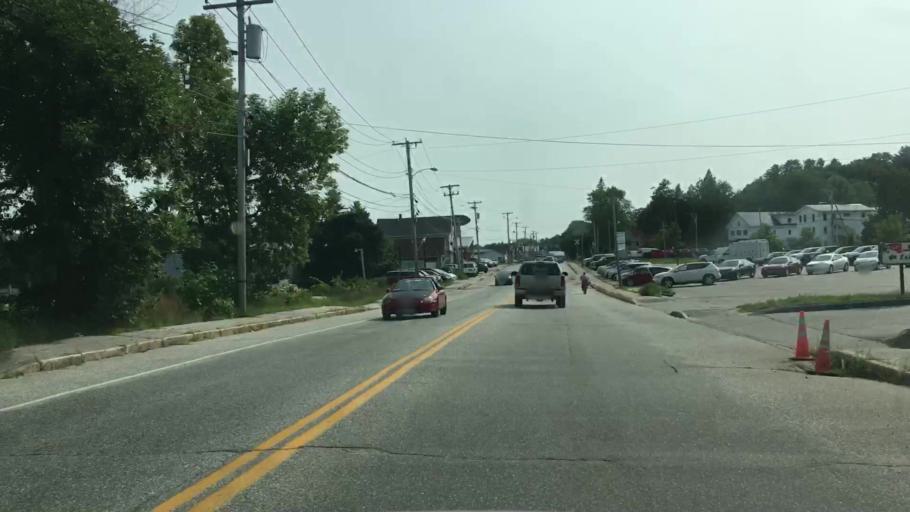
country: US
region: Maine
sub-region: Oxford County
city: South Paris
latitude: 44.2214
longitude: -70.5158
